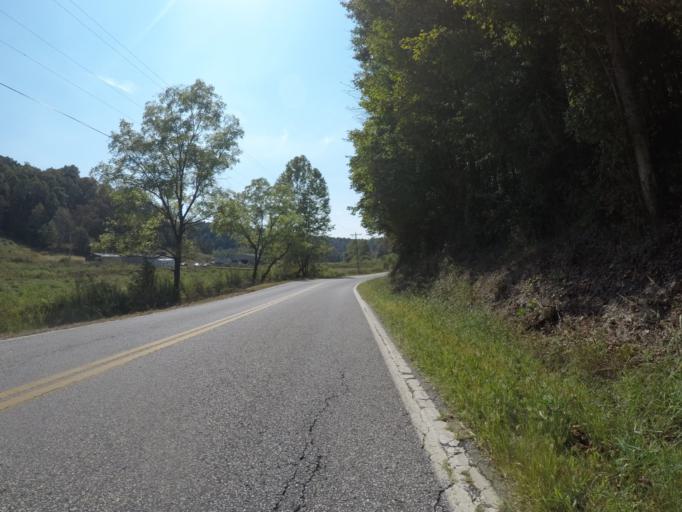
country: US
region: West Virginia
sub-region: Cabell County
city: Lesage
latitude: 38.5584
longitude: -82.3923
